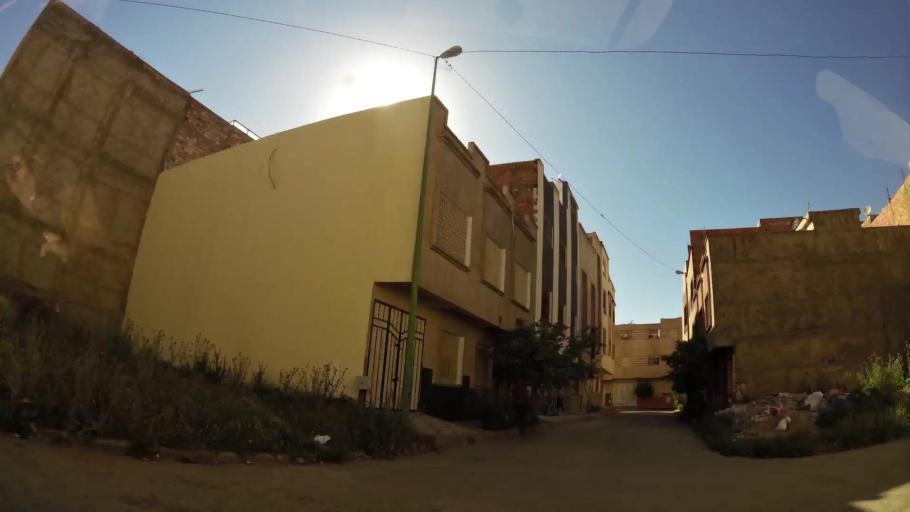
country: MA
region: Meknes-Tafilalet
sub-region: Meknes
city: Meknes
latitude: 33.8779
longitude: -5.5763
